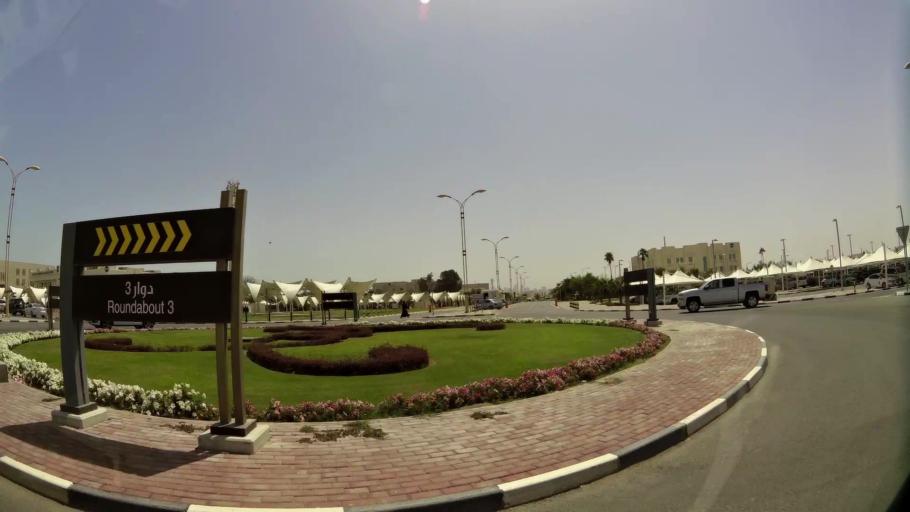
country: QA
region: Baladiyat Umm Salal
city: Umm Salal Muhammad
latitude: 25.3763
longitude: 51.4861
